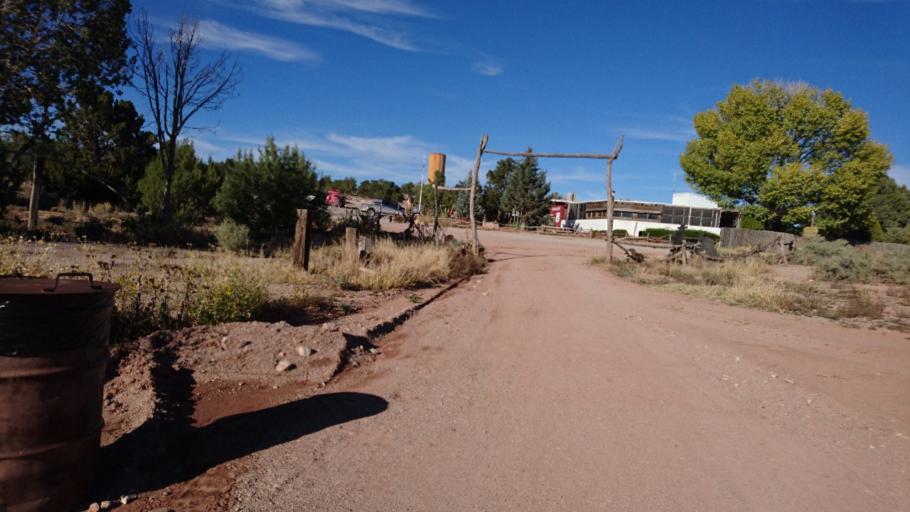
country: US
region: Arizona
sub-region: Mohave County
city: Peach Springs
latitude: 35.5171
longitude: -113.2194
